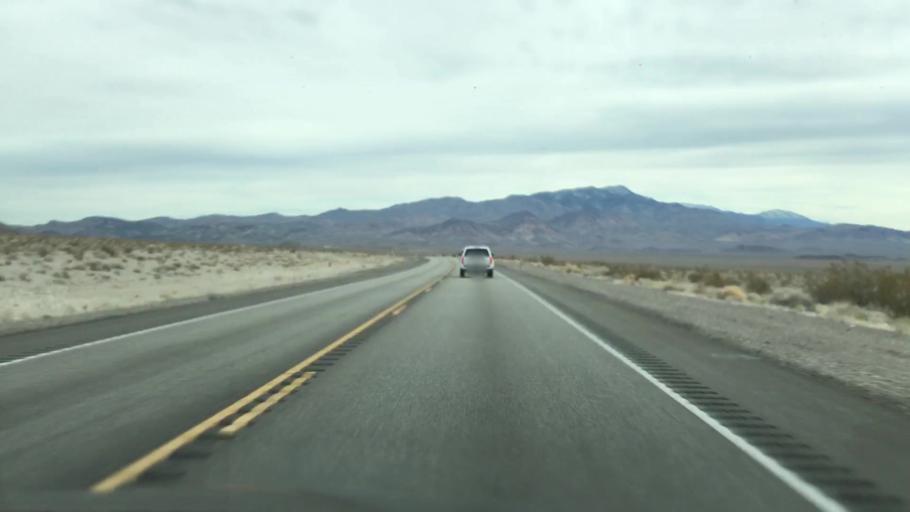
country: US
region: Nevada
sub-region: Nye County
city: Pahrump
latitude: 36.5753
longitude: -116.1895
